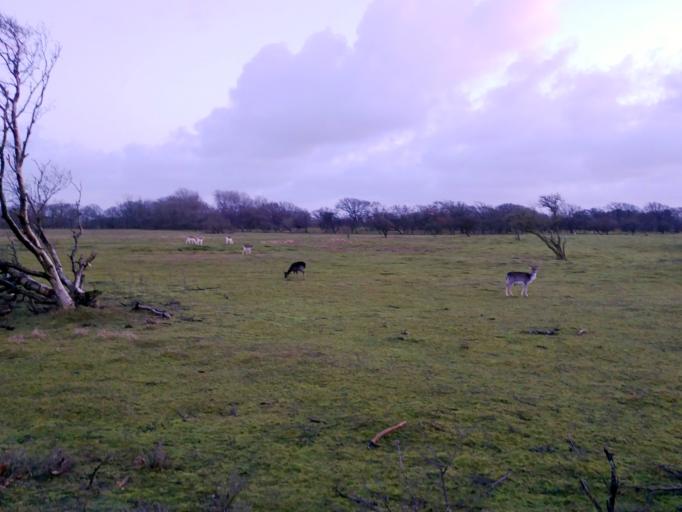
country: NL
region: South Holland
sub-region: Gemeente Hillegom
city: Hillegom
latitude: 52.3120
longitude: 4.5299
